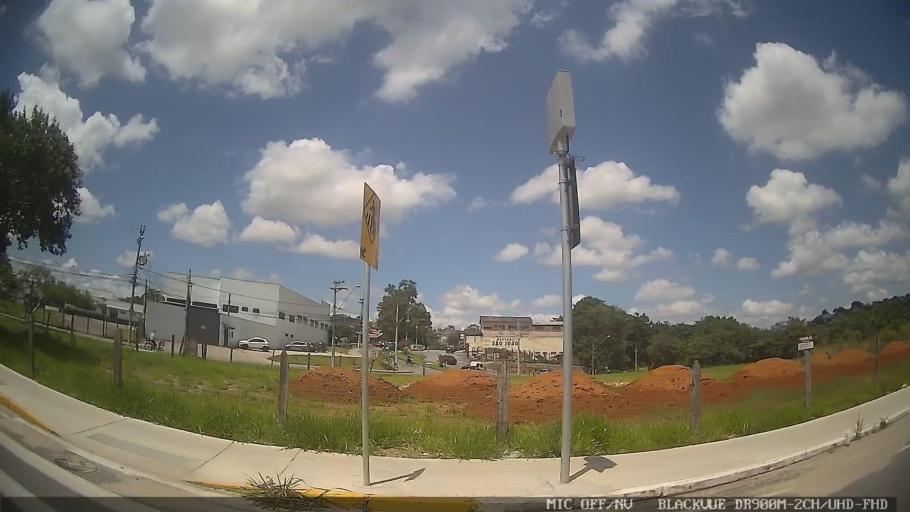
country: BR
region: Sao Paulo
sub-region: Jacarei
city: Jacarei
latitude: -23.3116
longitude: -45.9950
